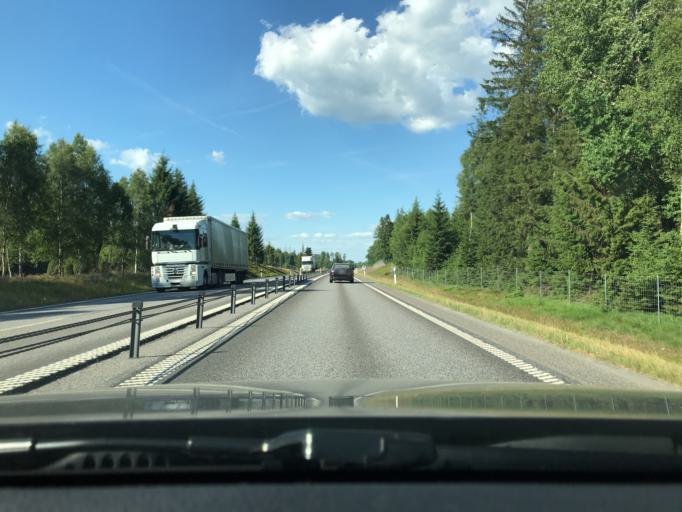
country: SE
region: Kronoberg
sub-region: Almhults Kommun
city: AElmhult
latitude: 56.5072
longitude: 14.1271
